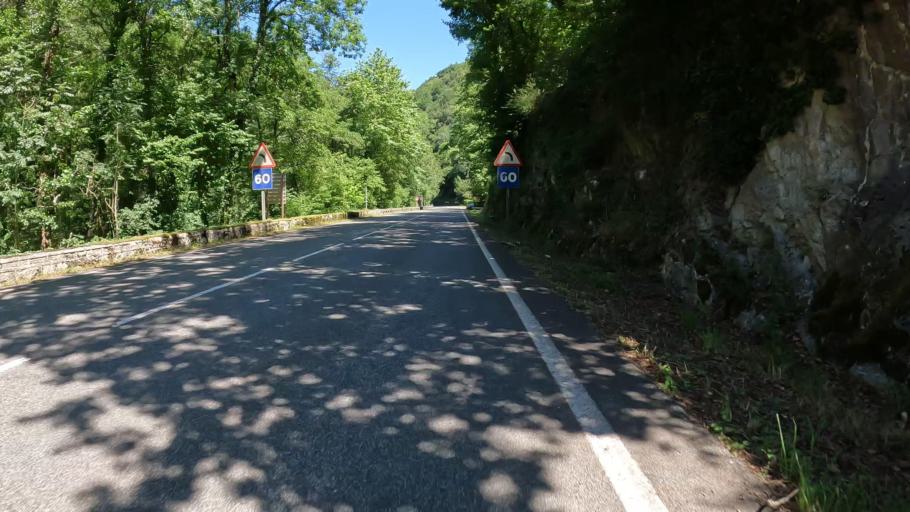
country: ES
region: Basque Country
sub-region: Provincia de Guipuzcoa
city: Oreja
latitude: 43.0722
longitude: -2.0116
